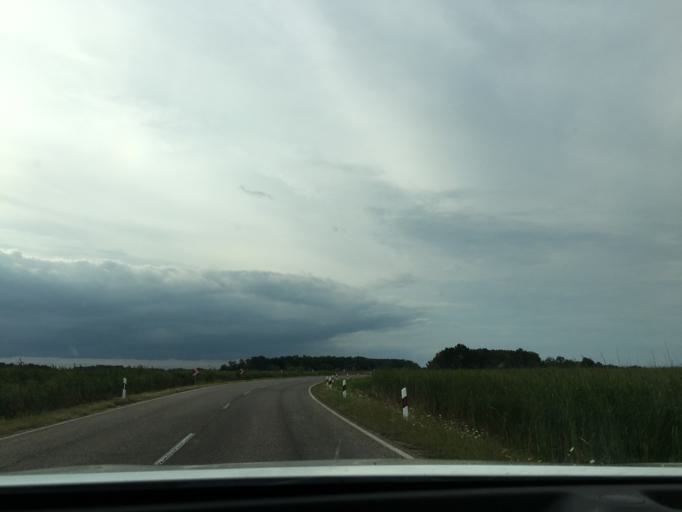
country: HU
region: Hajdu-Bihar
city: Egyek
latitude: 47.5588
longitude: 20.8658
